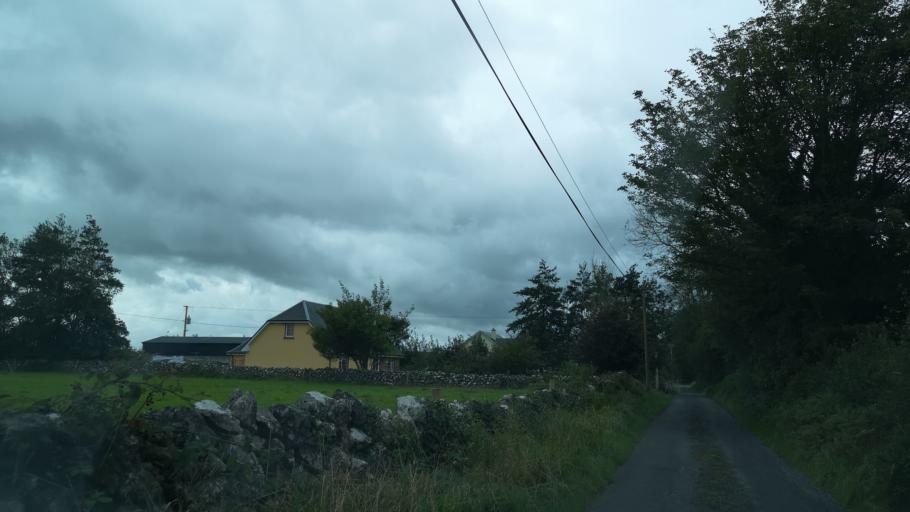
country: IE
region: Connaught
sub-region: County Galway
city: Athenry
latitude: 53.3295
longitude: -8.7610
